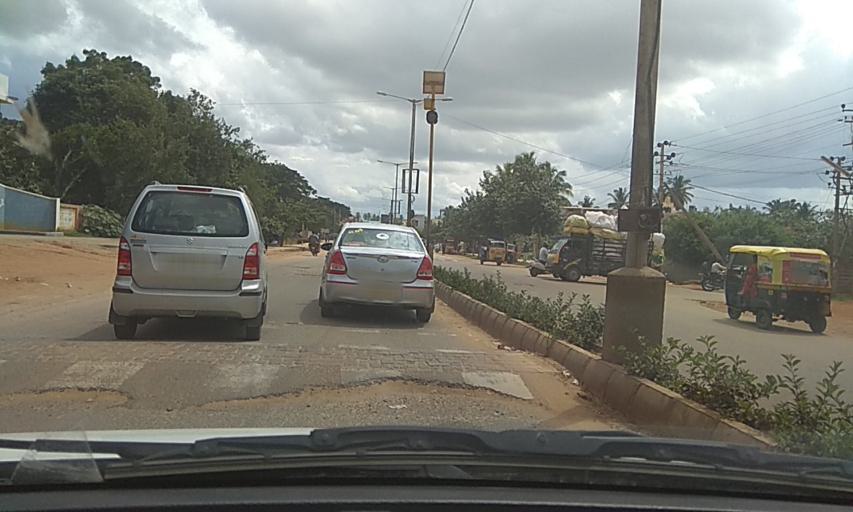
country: IN
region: Karnataka
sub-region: Tumkur
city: Tumkur
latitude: 13.3312
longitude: 77.0954
